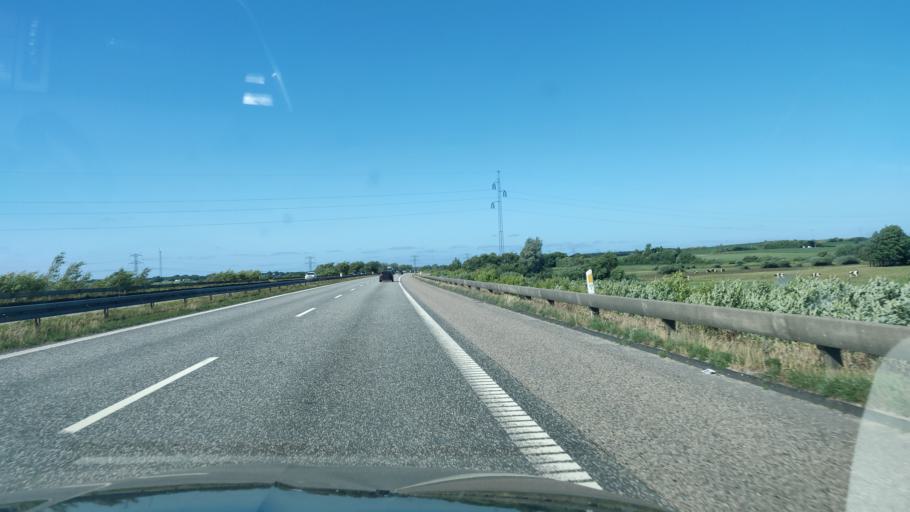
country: DK
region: North Denmark
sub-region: Rebild Kommune
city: Stovring
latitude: 56.8124
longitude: 9.7148
